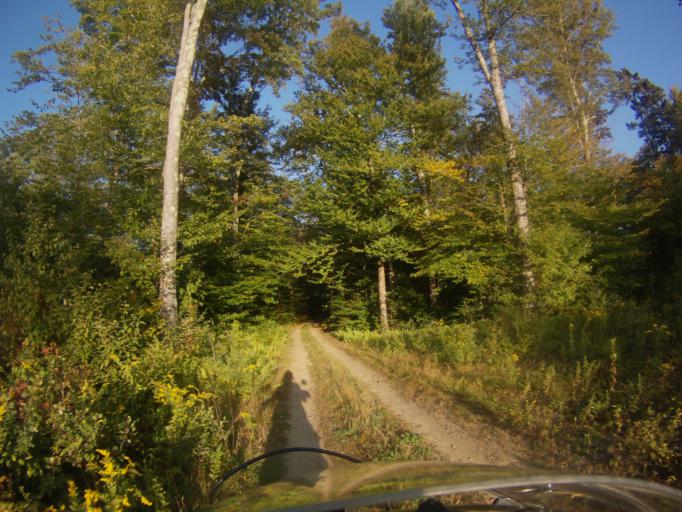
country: US
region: Vermont
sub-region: Addison County
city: Bristol
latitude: 44.0083
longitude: -73.0073
